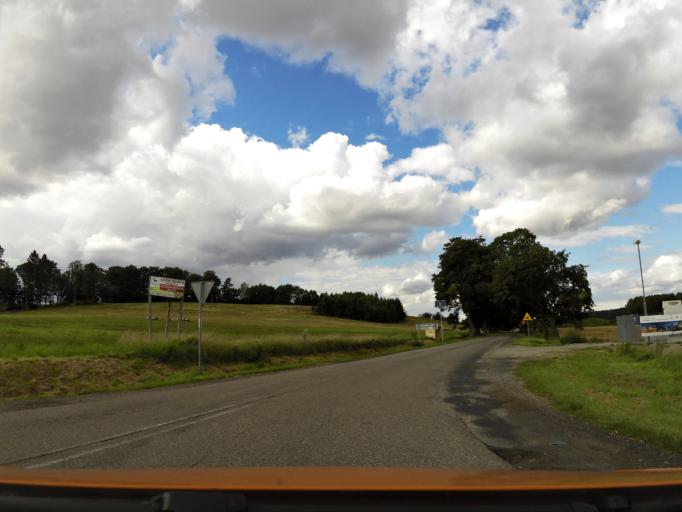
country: PL
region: West Pomeranian Voivodeship
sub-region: Powiat kolobrzeski
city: Ryman
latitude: 53.9335
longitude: 15.5017
